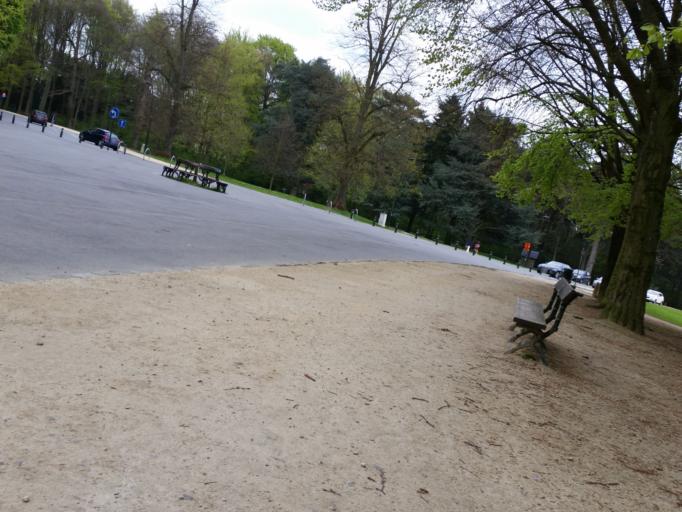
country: BE
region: Brussels Capital
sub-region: Bruxelles-Capitale
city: Brussels
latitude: 50.8071
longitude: 4.3797
